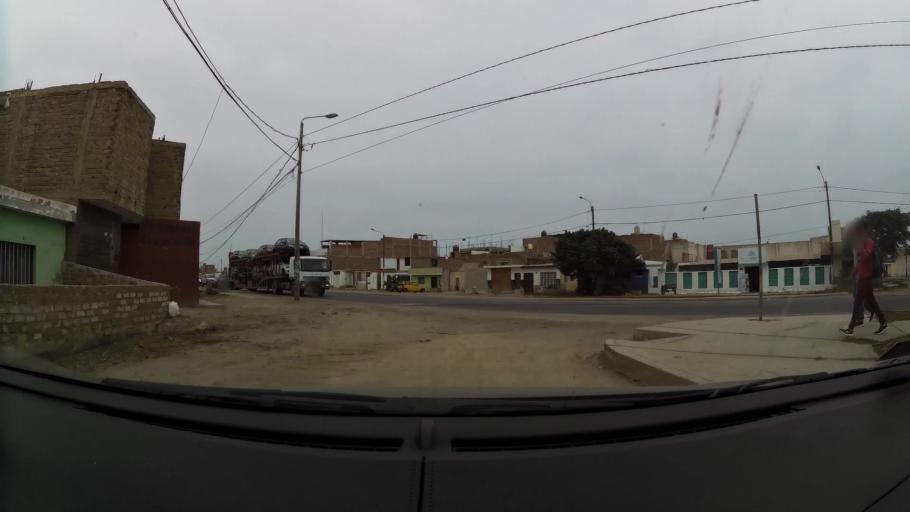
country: PE
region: La Libertad
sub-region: Provincia de Trujillo
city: Buenos Aires
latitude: -8.1419
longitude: -79.0508
